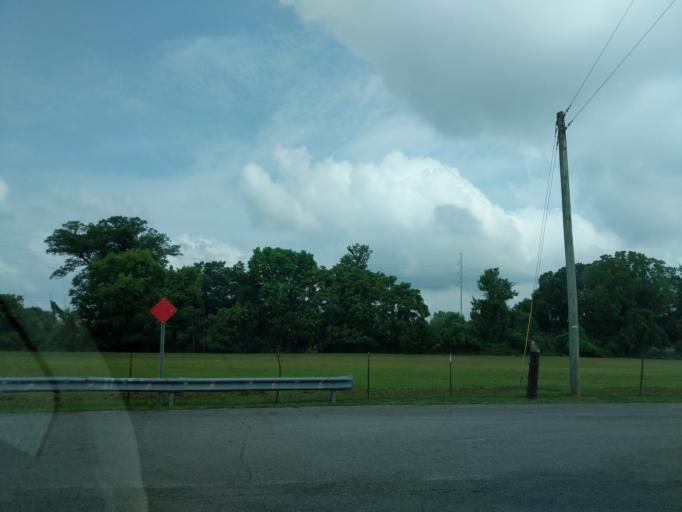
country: US
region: Tennessee
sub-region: Davidson County
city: Lakewood
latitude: 36.1884
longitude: -86.6120
